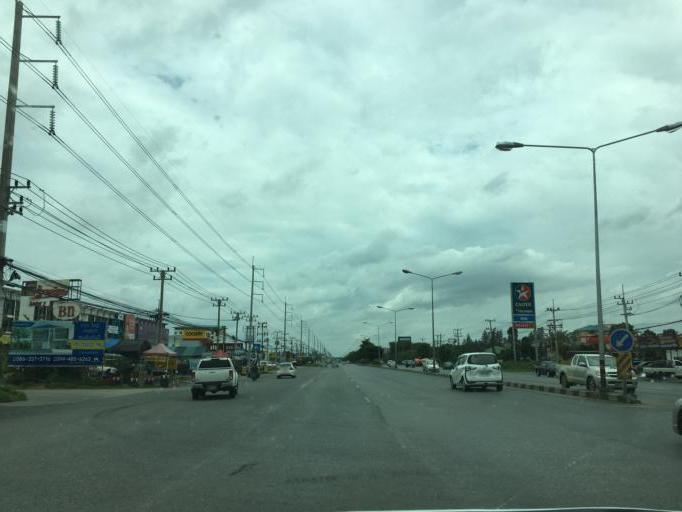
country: TH
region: Phra Nakhon Si Ayutthaya
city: Uthai
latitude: 14.3026
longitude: 100.6512
